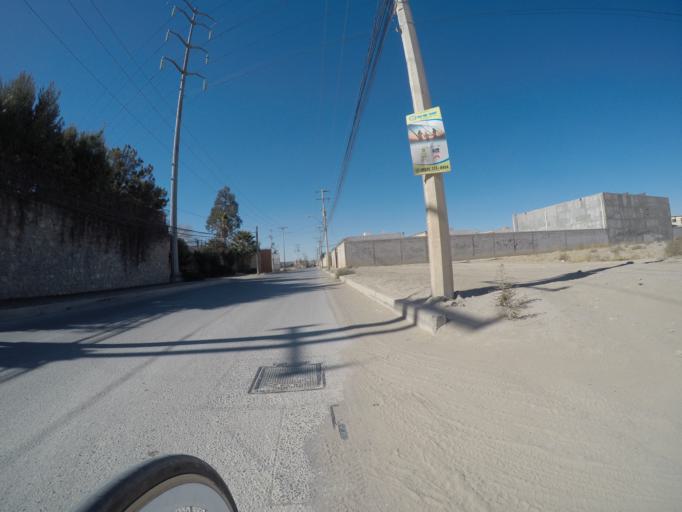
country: MX
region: Chihuahua
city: Ciudad Juarez
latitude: 31.6954
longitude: -106.4010
